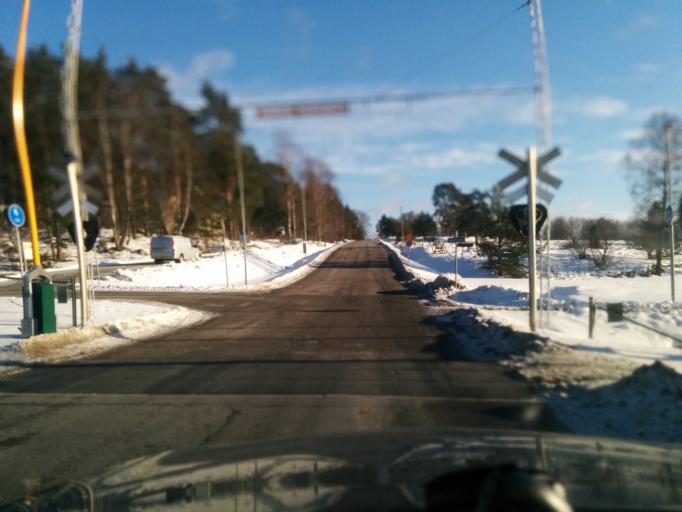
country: SE
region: Stockholm
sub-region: Vallentuna Kommun
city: Vallentuna
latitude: 59.4903
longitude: 18.0632
